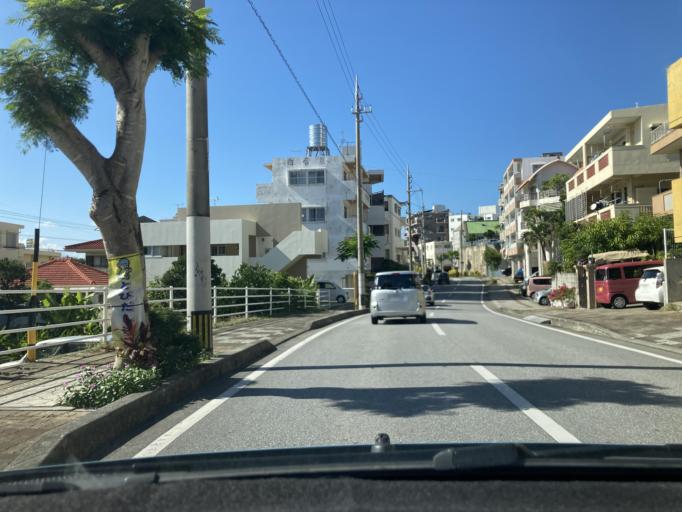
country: JP
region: Okinawa
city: Naha-shi
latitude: 26.2367
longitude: 127.7020
